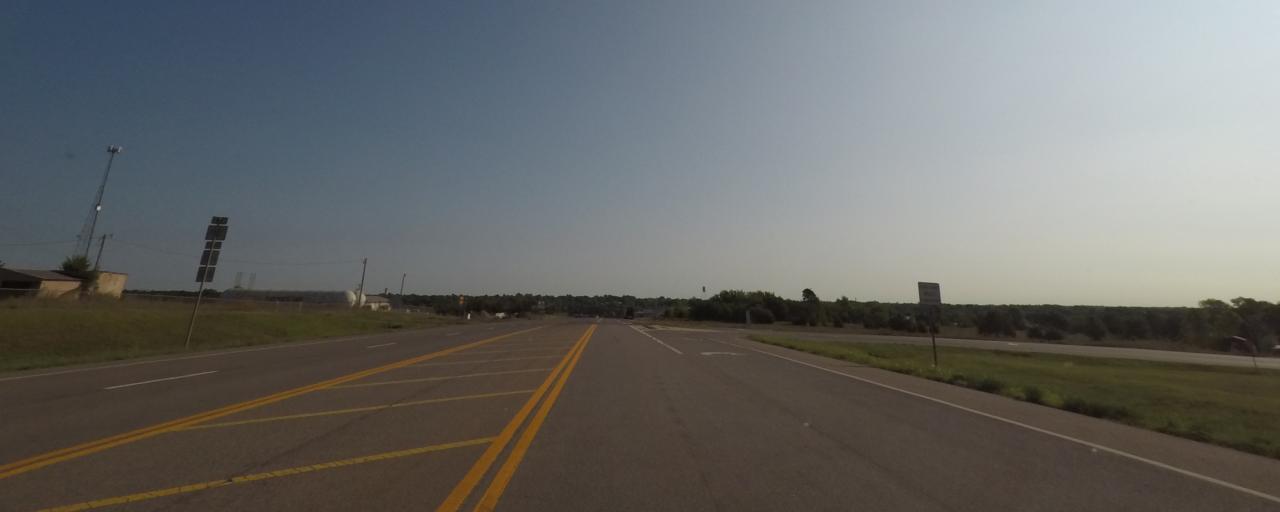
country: US
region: Oklahoma
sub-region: McClain County
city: Blanchard
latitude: 35.1273
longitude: -97.6701
